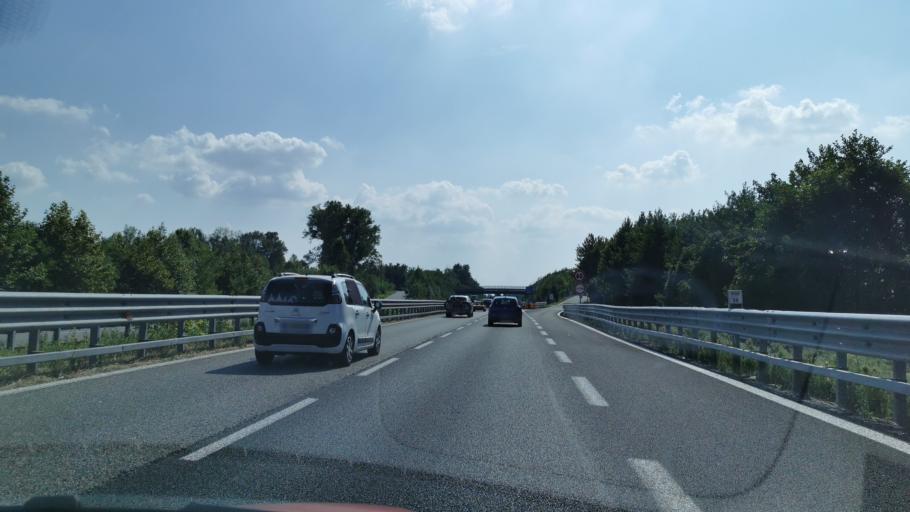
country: IT
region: Lombardy
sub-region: Provincia di Lecco
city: Bosisio Parini
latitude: 45.7980
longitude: 9.3048
